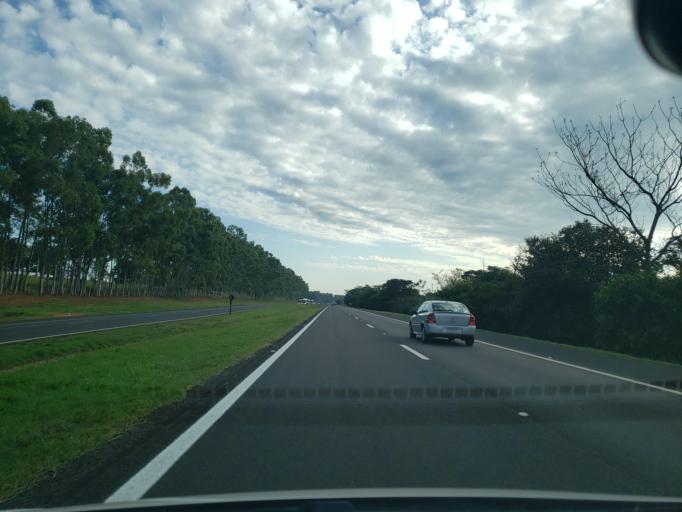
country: BR
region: Sao Paulo
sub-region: Guararapes
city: Guararapes
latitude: -21.2114
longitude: -50.6743
